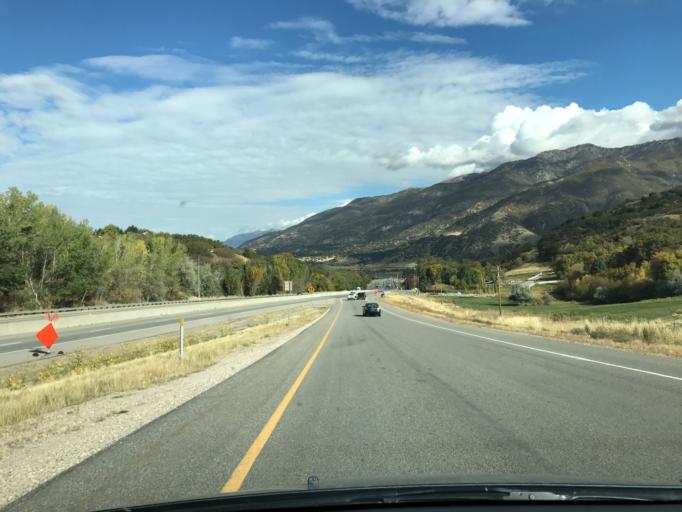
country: US
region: Utah
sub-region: Davis County
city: South Weber
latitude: 41.1091
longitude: -111.9092
